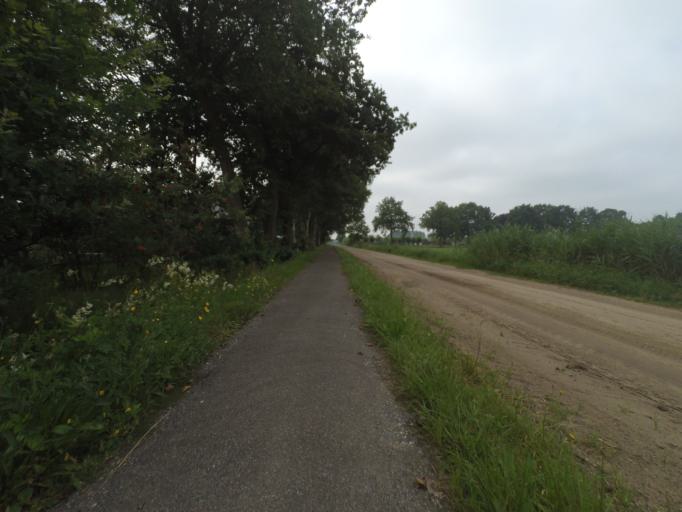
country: NL
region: Gelderland
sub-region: Gemeente Barneveld
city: Kootwijkerbroek
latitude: 52.1219
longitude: 5.6571
